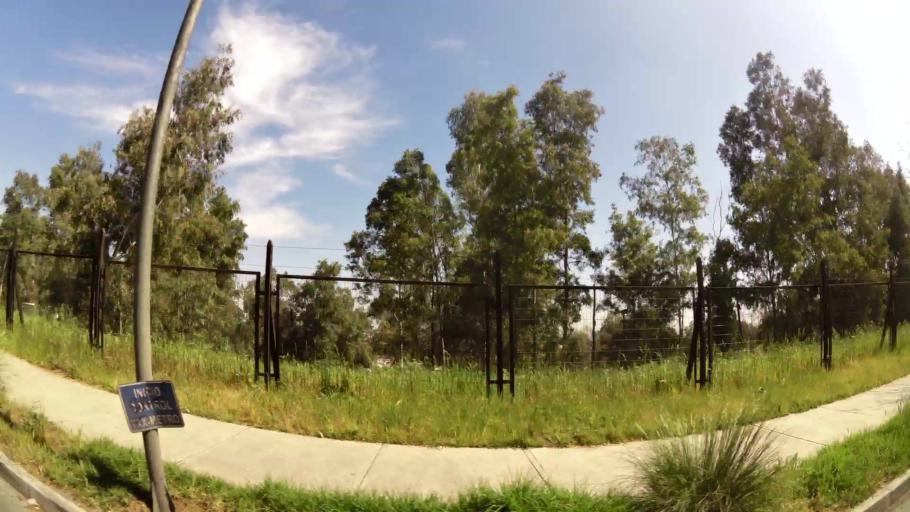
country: CL
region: Santiago Metropolitan
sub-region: Provincia de Santiago
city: Villa Presidente Frei, Nunoa, Santiago, Chile
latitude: -33.4539
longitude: -70.5289
